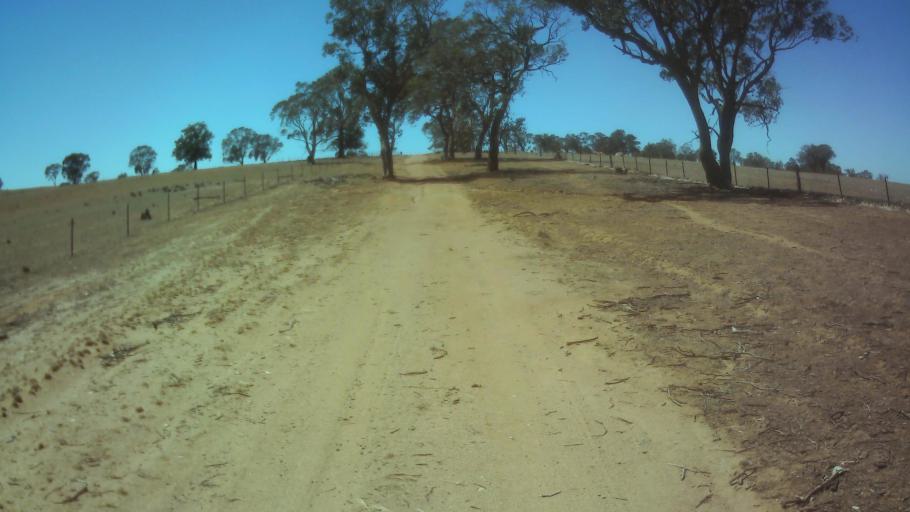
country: AU
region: New South Wales
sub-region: Cowra
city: Cowra
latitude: -33.8989
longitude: 148.5072
